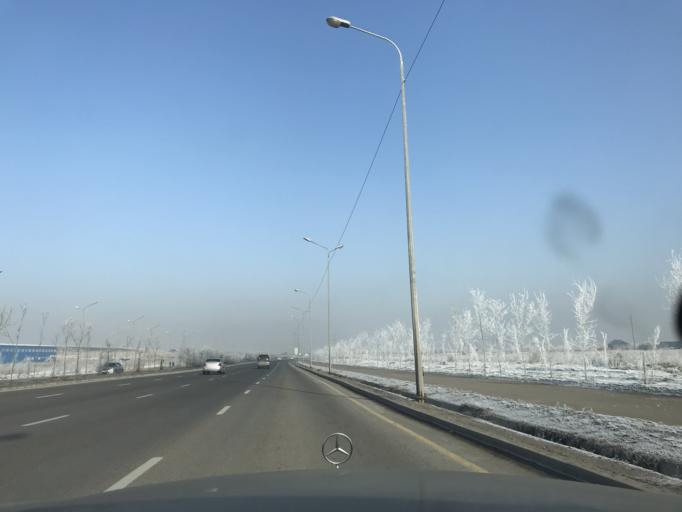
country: KZ
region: Almaty Oblysy
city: Burunday
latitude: 43.3293
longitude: 76.8339
